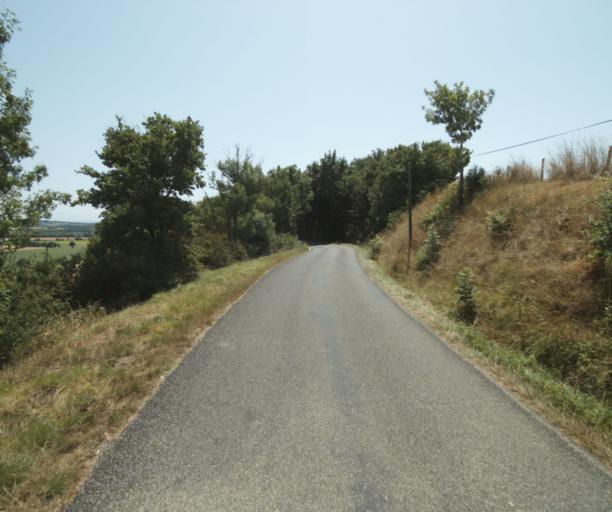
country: FR
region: Midi-Pyrenees
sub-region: Departement de la Haute-Garonne
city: Saint-Felix-Lauragais
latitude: 43.4413
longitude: 1.8946
